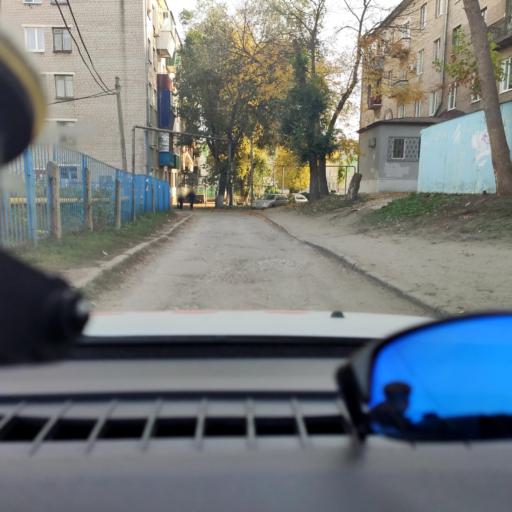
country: RU
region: Samara
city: Samara
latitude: 53.2136
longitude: 50.2425
